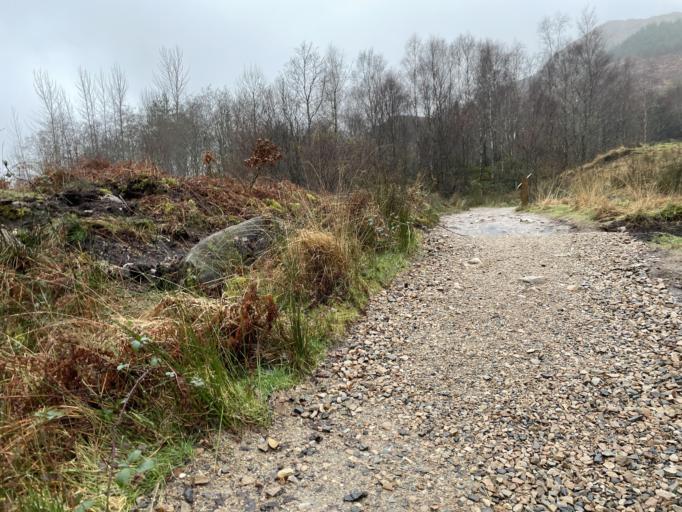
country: GB
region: Scotland
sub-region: Highland
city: Fort William
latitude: 56.8755
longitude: -5.4323
